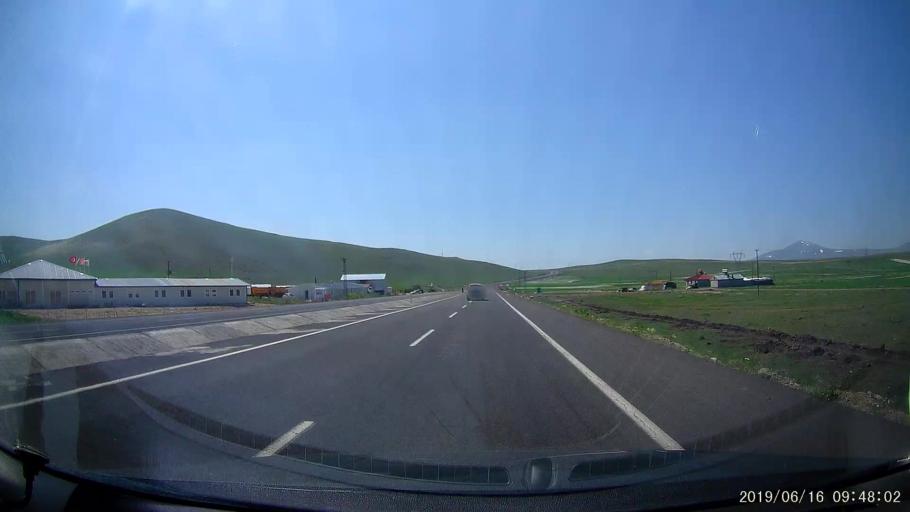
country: TR
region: Kars
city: Digor
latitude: 40.4379
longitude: 43.3503
